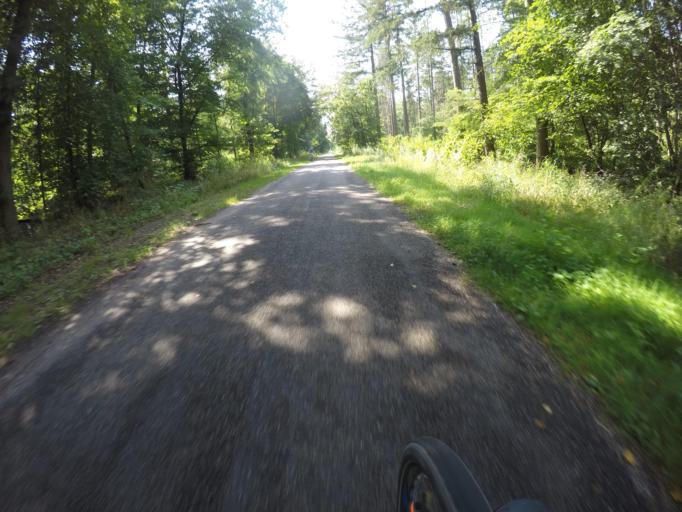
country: DE
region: Baden-Wuerttemberg
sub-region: Karlsruhe Region
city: Forst
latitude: 49.1734
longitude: 8.5924
